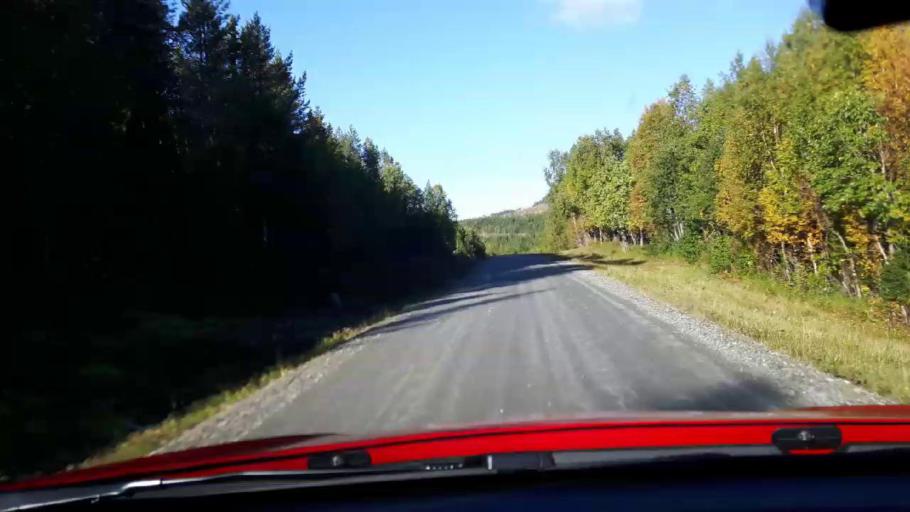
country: NO
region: Nord-Trondelag
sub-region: Lierne
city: Sandvika
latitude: 64.5877
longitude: 13.8671
